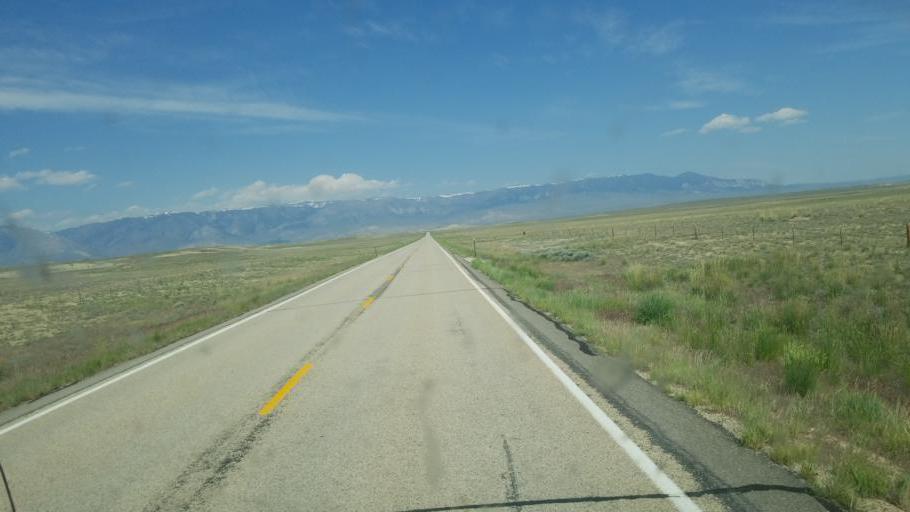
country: US
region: Wyoming
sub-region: Park County
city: Powell
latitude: 44.8615
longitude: -109.0282
